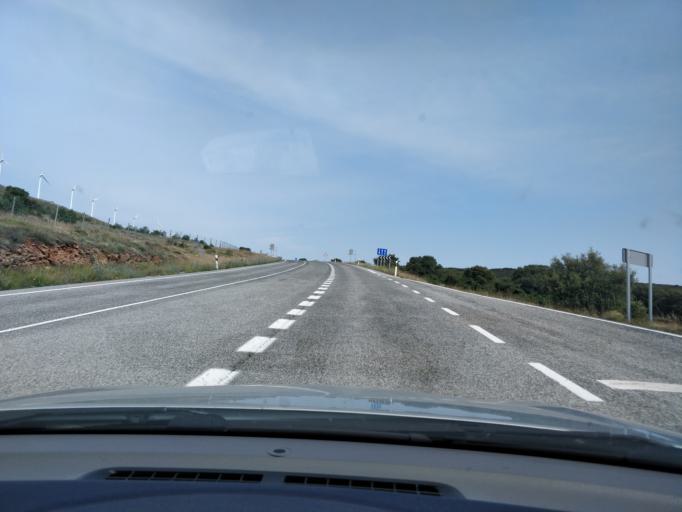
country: ES
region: Castille and Leon
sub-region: Provincia de Burgos
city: Medina de Pomar
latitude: 42.9247
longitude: -3.6307
